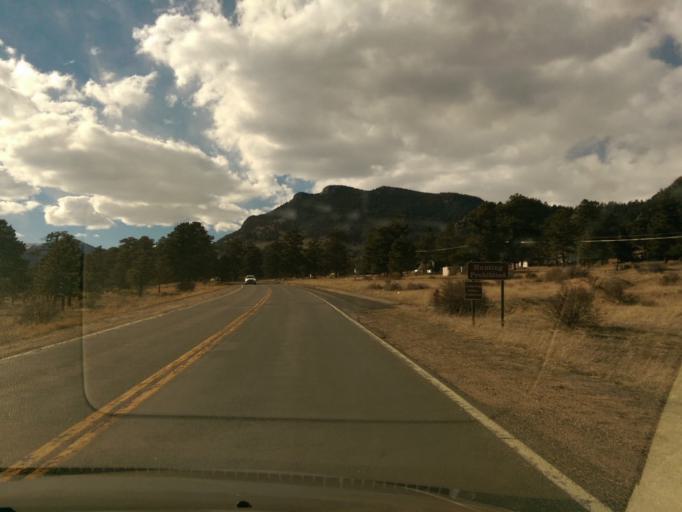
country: US
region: Colorado
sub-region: Larimer County
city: Estes Park
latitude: 40.3645
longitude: -105.5517
